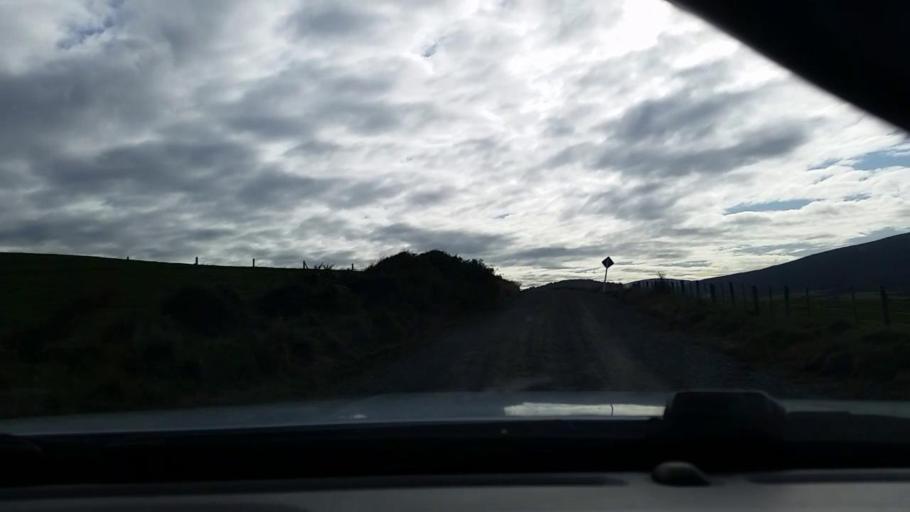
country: NZ
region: Southland
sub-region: Southland District
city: Riverton
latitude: -46.3293
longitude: 167.7993
